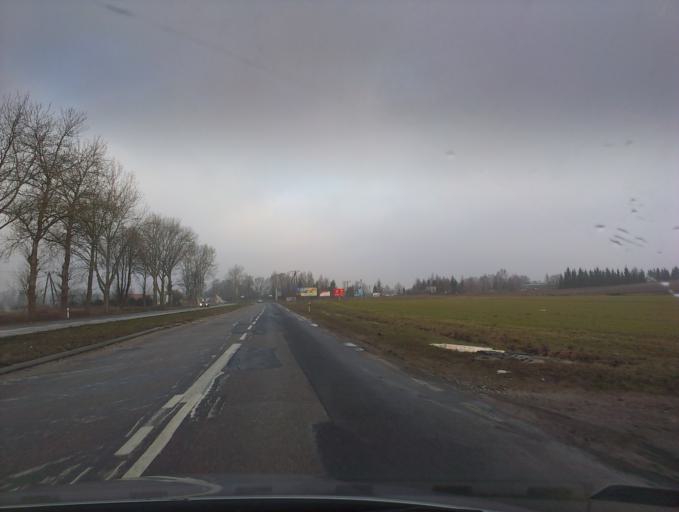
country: PL
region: West Pomeranian Voivodeship
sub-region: Koszalin
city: Koszalin
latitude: 54.1601
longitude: 16.2255
